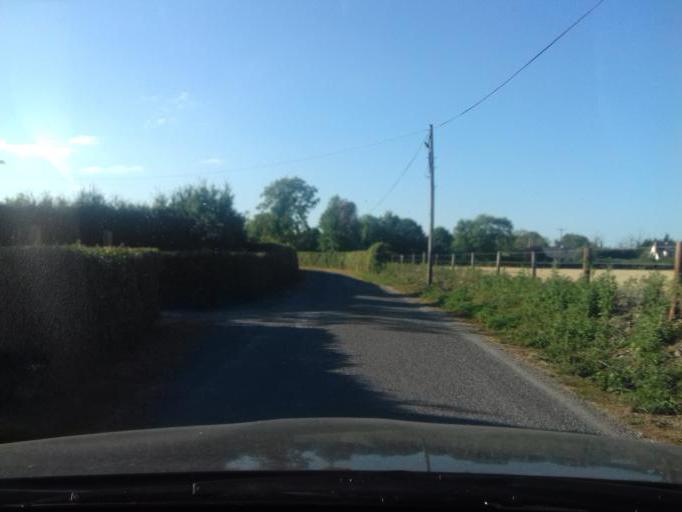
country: IE
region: Leinster
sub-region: An Mhi
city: Ashbourne
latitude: 53.4525
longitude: -6.3794
